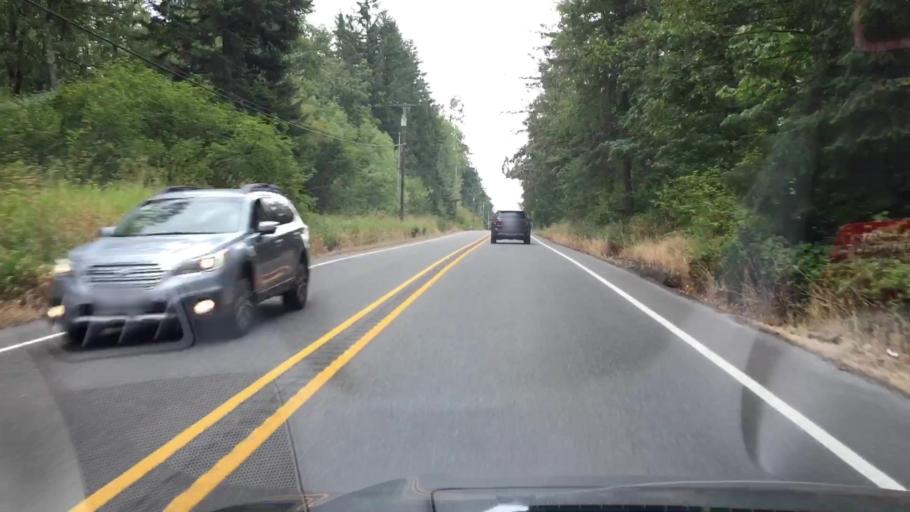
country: US
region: Washington
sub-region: Pierce County
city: Graham
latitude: 46.9619
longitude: -122.2976
